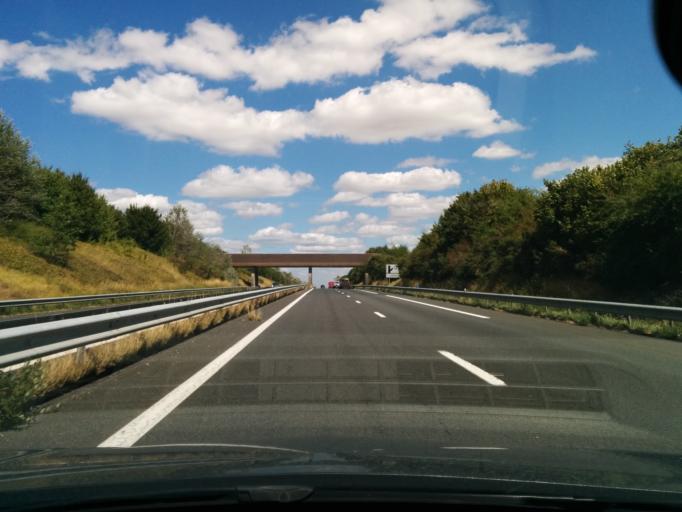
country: FR
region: Centre
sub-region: Departement du Cher
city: Massay
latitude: 47.1294
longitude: 1.9410
